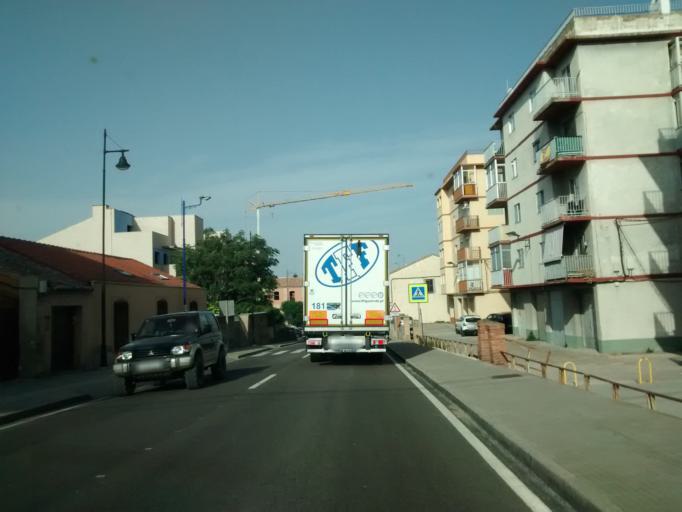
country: ES
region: Aragon
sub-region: Provincia de Zaragoza
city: Borja
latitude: 41.8312
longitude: -1.5348
